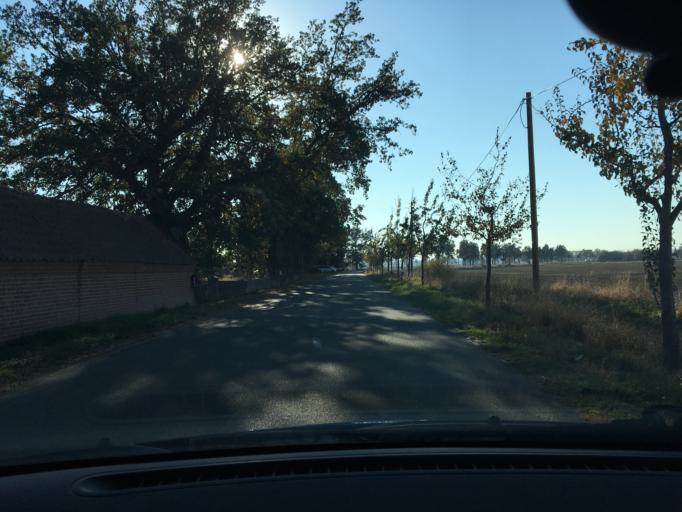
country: DE
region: Lower Saxony
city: Damnatz
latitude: 53.1653
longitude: 11.1220
